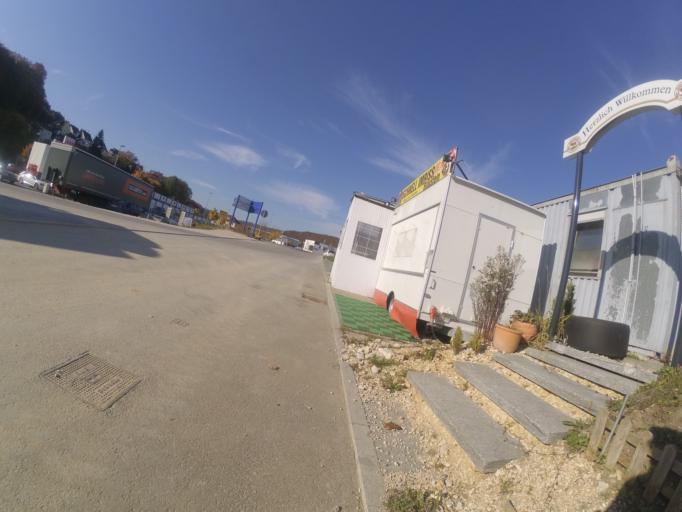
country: DE
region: Baden-Wuerttemberg
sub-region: Tuebingen Region
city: Dornstadt
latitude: 48.4115
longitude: 9.9225
